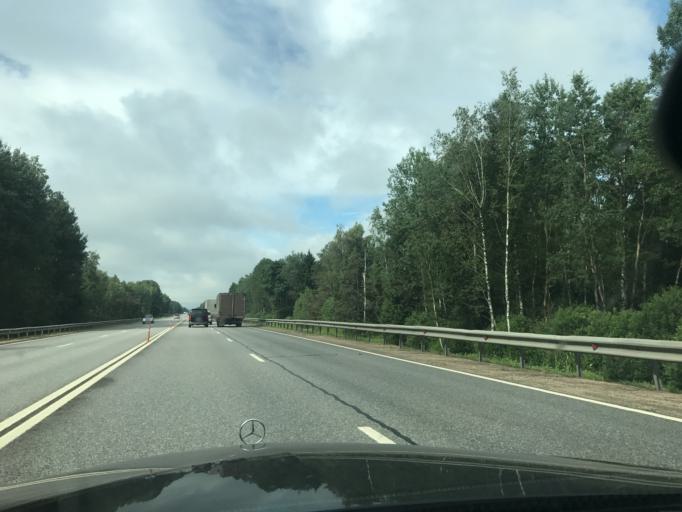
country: RU
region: Smolensk
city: Kardymovo
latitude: 55.0070
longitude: 32.2843
